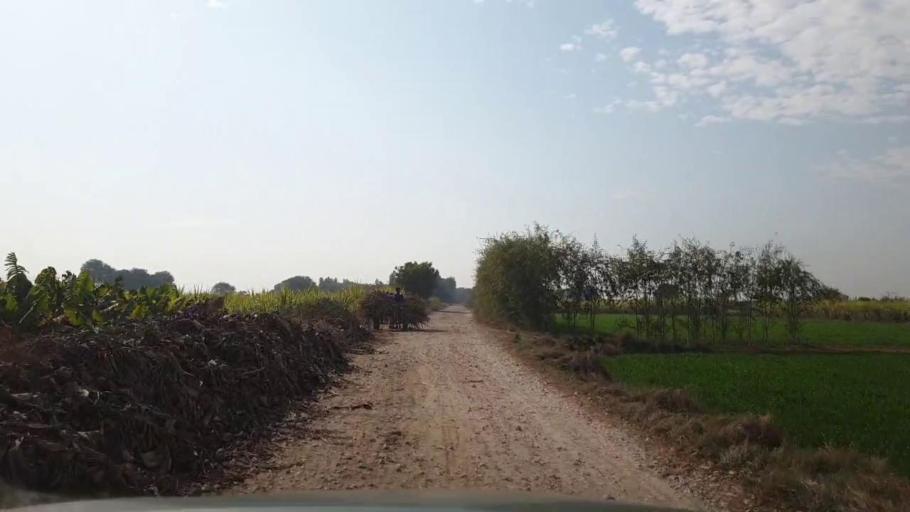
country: PK
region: Sindh
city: Matiari
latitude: 25.5607
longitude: 68.5200
